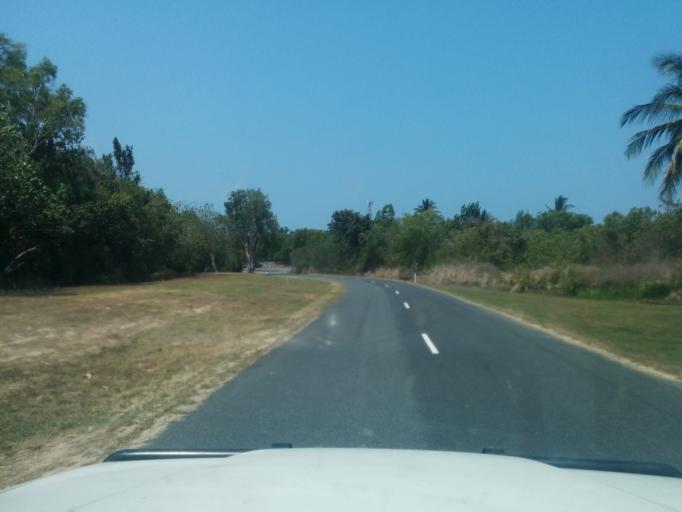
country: AU
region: Queensland
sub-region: Cairns
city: Redlynch
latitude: -16.8718
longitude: 145.7357
